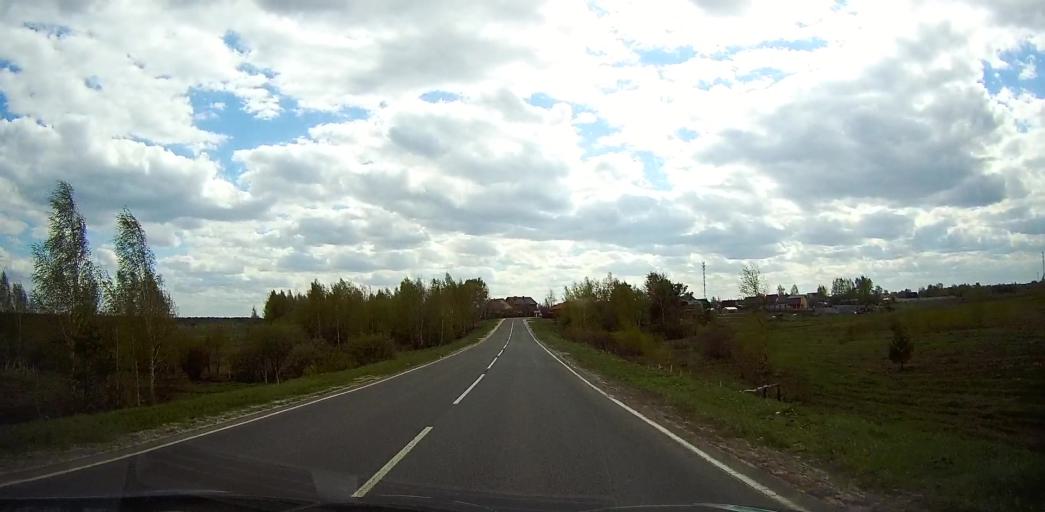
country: RU
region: Moskovskaya
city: Davydovo
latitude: 55.6333
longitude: 38.7457
